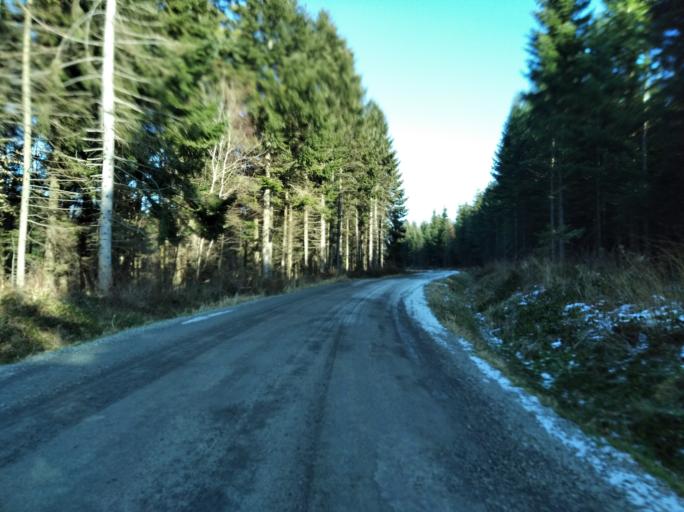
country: PL
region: Subcarpathian Voivodeship
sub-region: Powiat rzeszowski
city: Straszydle
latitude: 49.8734
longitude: 21.9774
